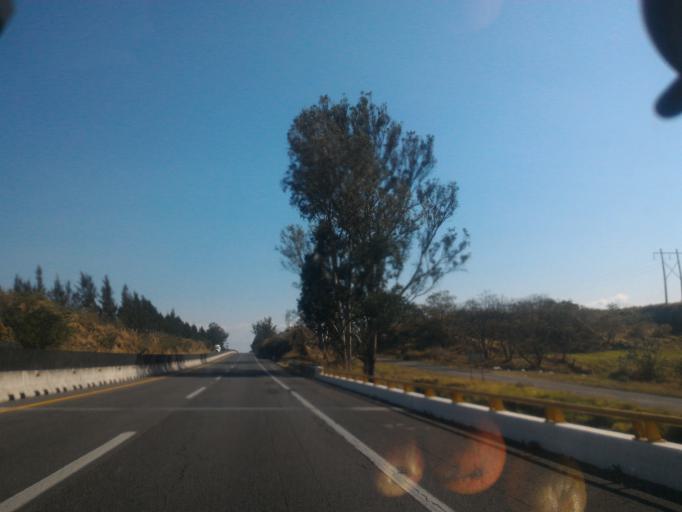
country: MX
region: Jalisco
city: Zapotiltic
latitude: 19.6232
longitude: -103.4632
